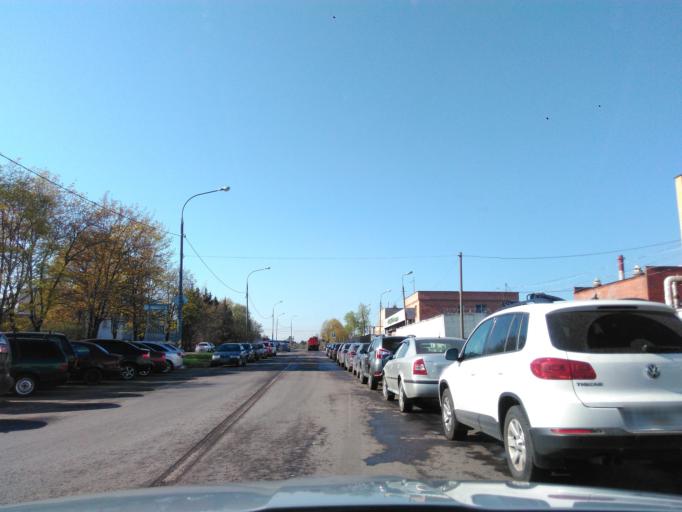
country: RU
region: Moskovskaya
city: Rzhavki
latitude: 55.9827
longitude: 37.2554
